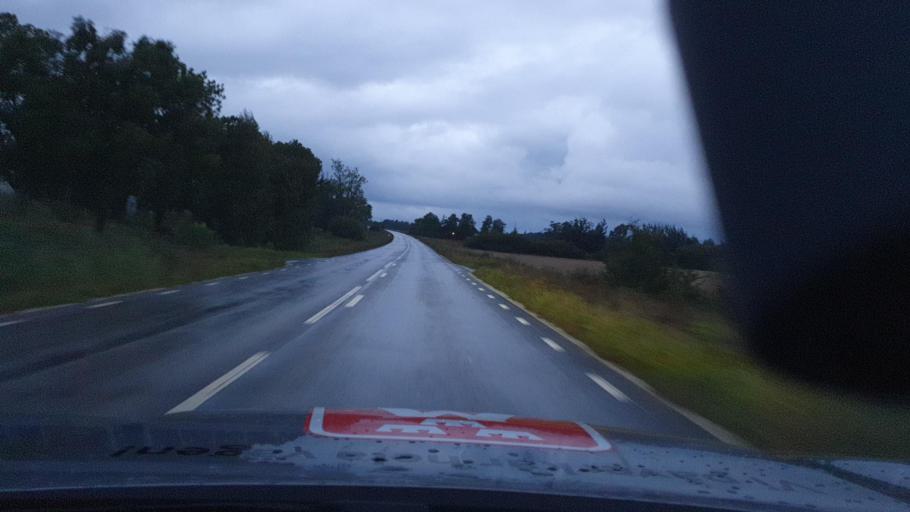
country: SE
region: Gotland
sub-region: Gotland
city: Slite
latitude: 57.7594
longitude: 18.7903
